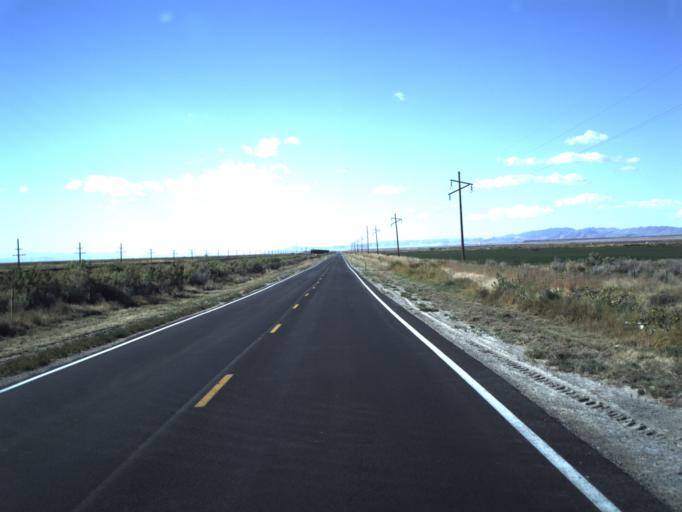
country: US
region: Utah
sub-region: Millard County
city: Delta
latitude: 39.2503
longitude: -112.6567
